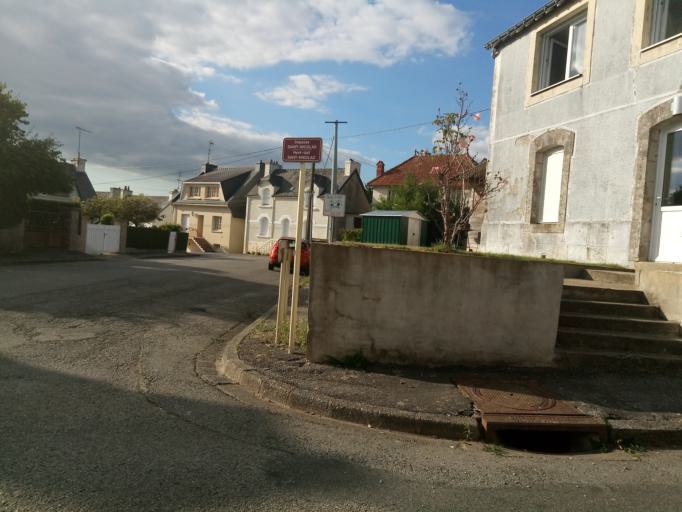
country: FR
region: Brittany
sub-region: Departement du Morbihan
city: Gourin
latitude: 48.1449
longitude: -3.5995
